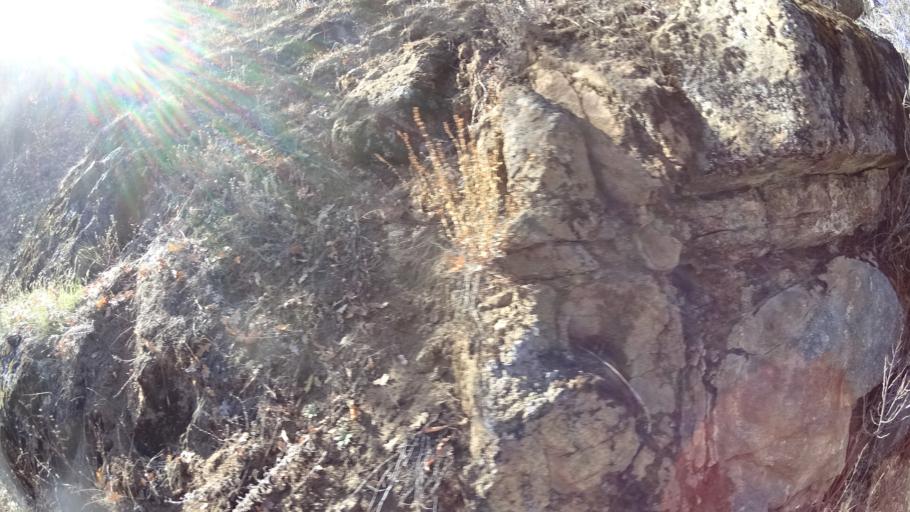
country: US
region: California
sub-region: Siskiyou County
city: Yreka
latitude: 41.8635
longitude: -122.7372
